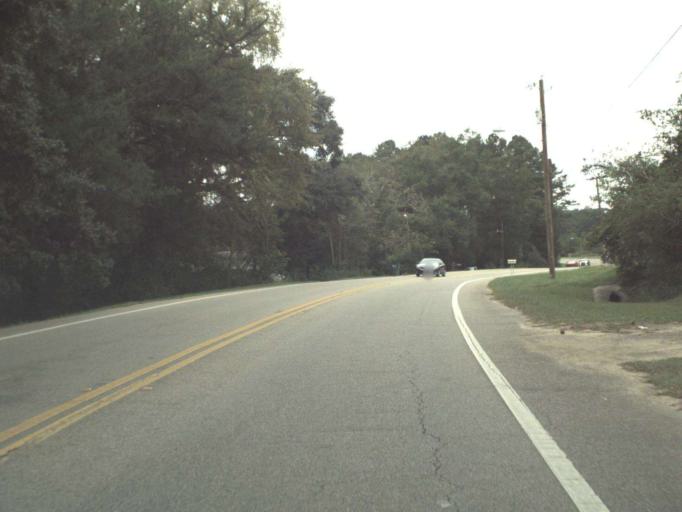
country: US
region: Florida
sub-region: Jackson County
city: Marianna
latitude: 30.7673
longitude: -85.2272
